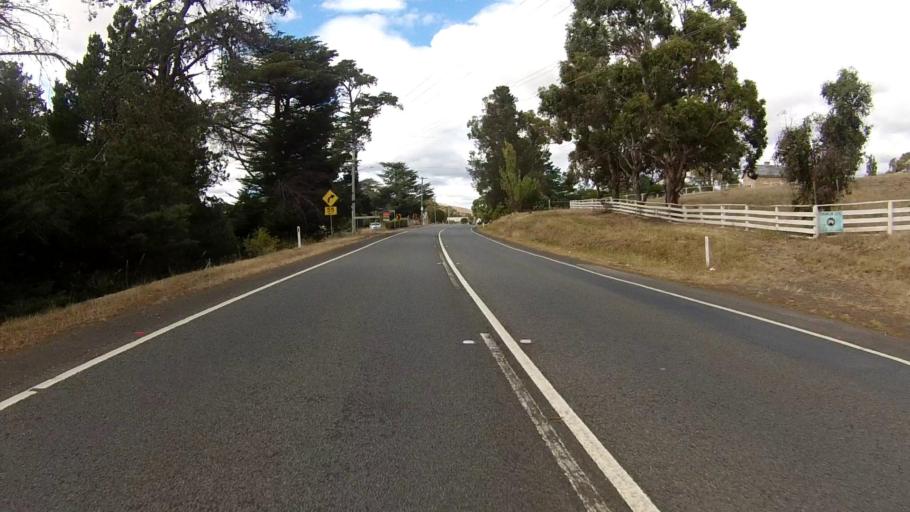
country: AU
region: Tasmania
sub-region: Brighton
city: Bridgewater
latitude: -42.6789
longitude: 147.2652
